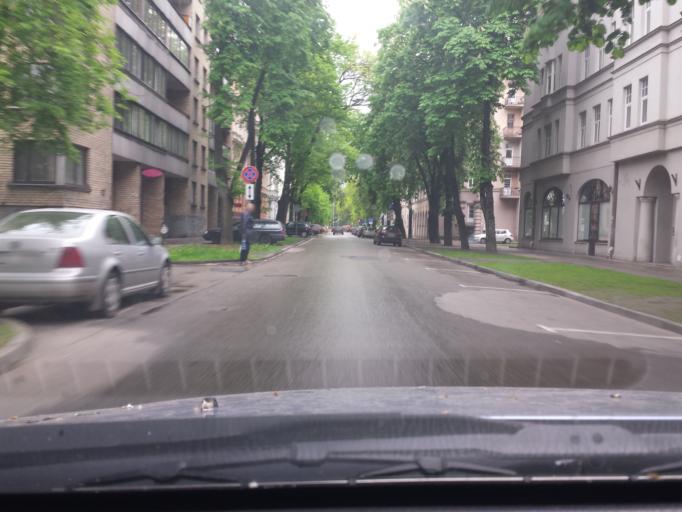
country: LV
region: Riga
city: Riga
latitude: 56.9610
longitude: 24.1001
